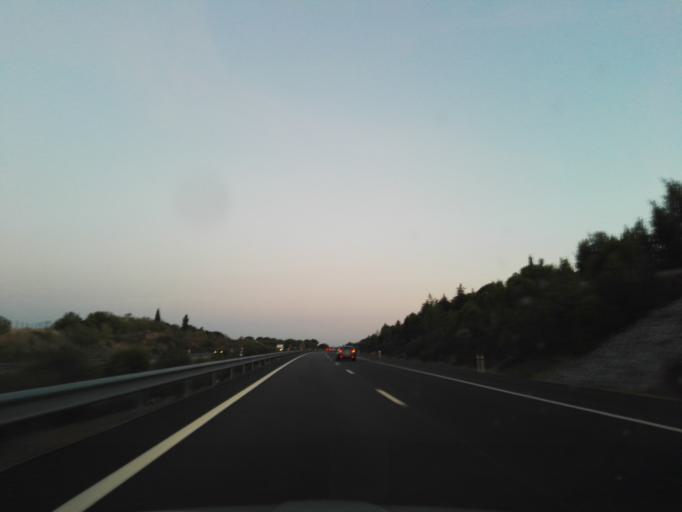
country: PT
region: Setubal
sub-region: Alcacer do Sal
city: Alcacer do Sal
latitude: 38.4715
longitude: -8.5326
